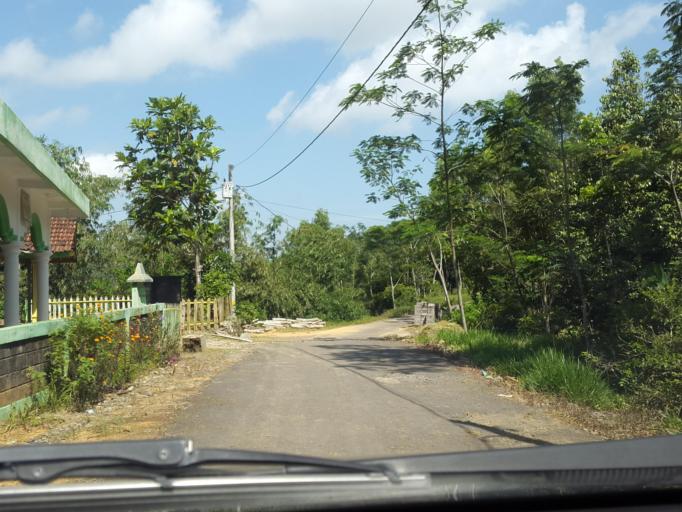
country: ID
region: Central Java
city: Selogiri
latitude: -7.9045
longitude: 110.7659
